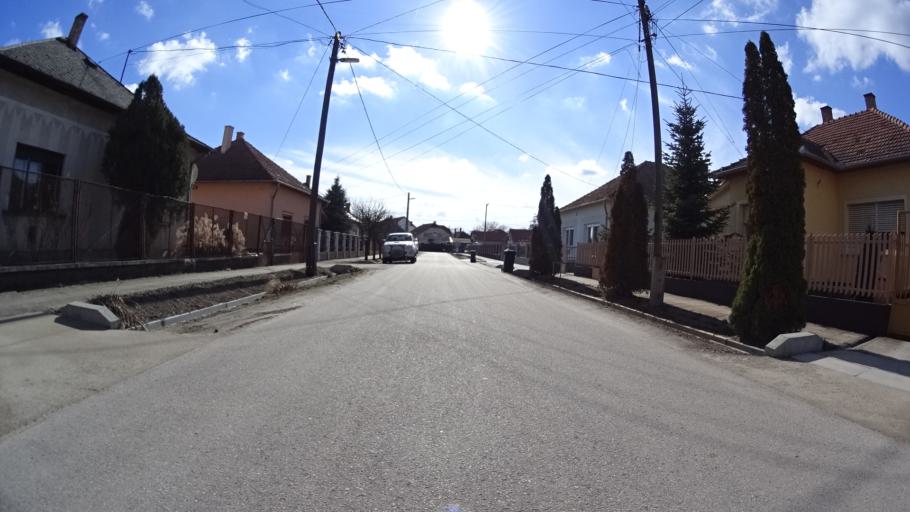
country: HU
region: Bacs-Kiskun
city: Tiszakecske
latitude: 46.9356
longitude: 20.0973
